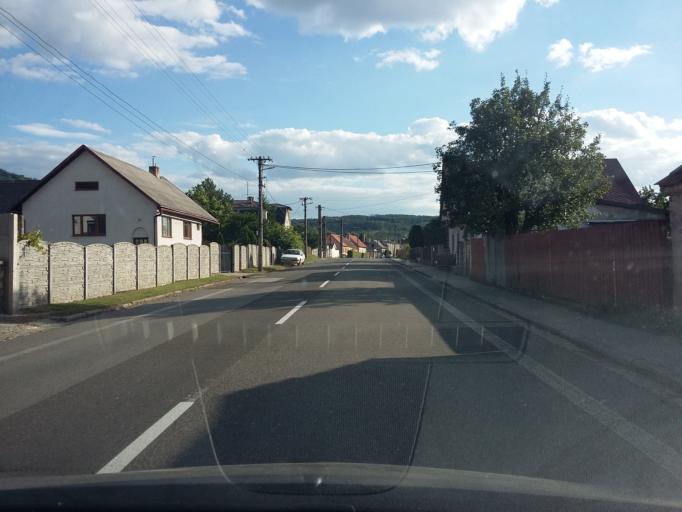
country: SK
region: Bratislavsky
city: Modra
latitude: 48.4675
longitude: 17.2342
